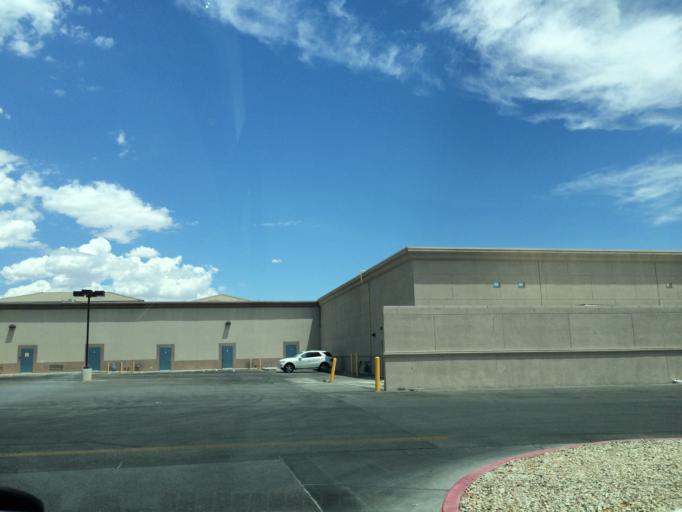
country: US
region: Nevada
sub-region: Clark County
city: North Las Vegas
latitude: 36.2608
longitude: -115.1823
